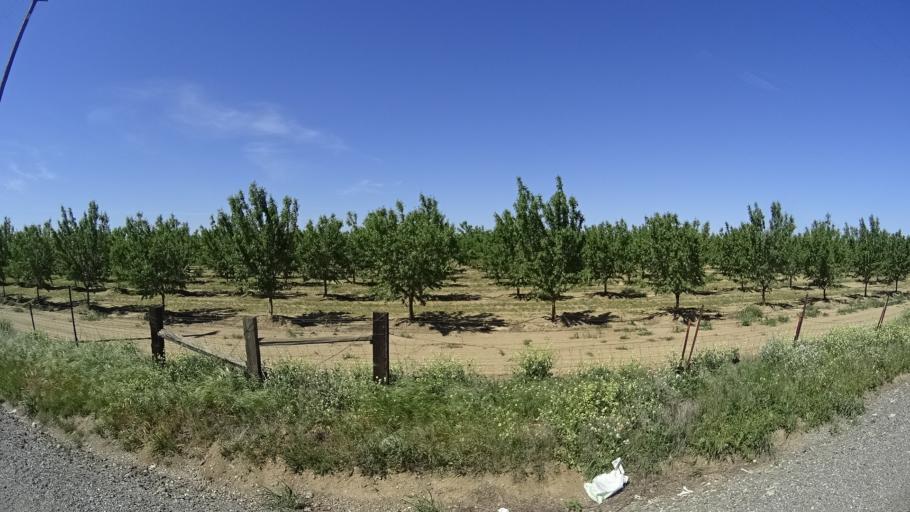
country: US
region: California
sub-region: Glenn County
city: Orland
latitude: 39.6632
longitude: -122.1407
